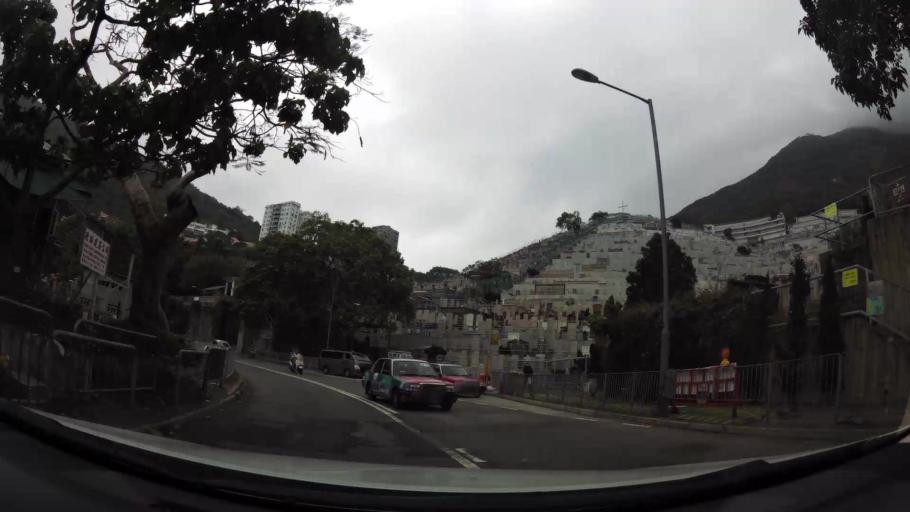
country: HK
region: Central and Western
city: Central
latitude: 22.2723
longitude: 114.1277
